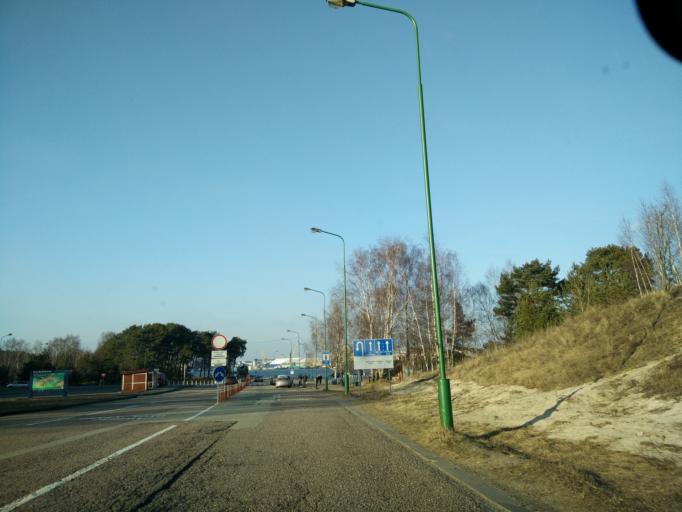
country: LT
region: Klaipedos apskritis
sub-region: Klaipeda
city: Klaipeda
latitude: 55.6842
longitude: 21.1297
